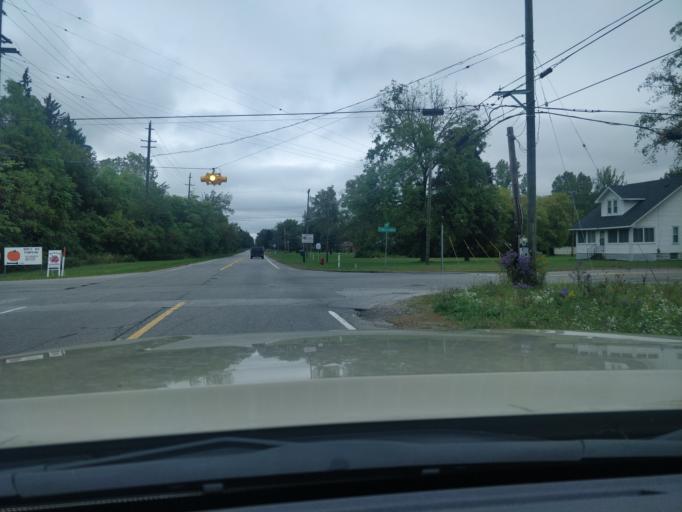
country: US
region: Michigan
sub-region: Wayne County
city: Romulus
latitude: 42.1795
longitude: -83.4035
